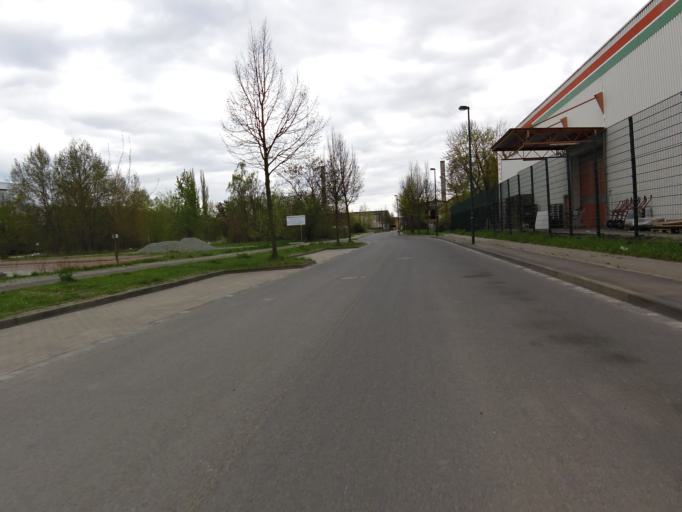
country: DE
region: Saxony
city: Markkleeberg
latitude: 51.2994
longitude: 12.3188
